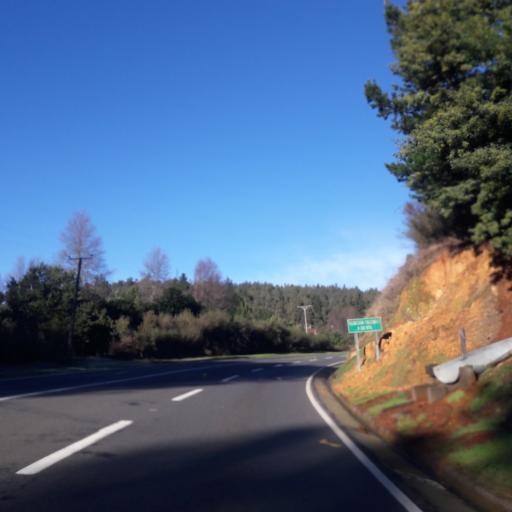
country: CL
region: Biobio
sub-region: Provincia de Biobio
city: La Laja
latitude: -37.2660
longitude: -72.9604
